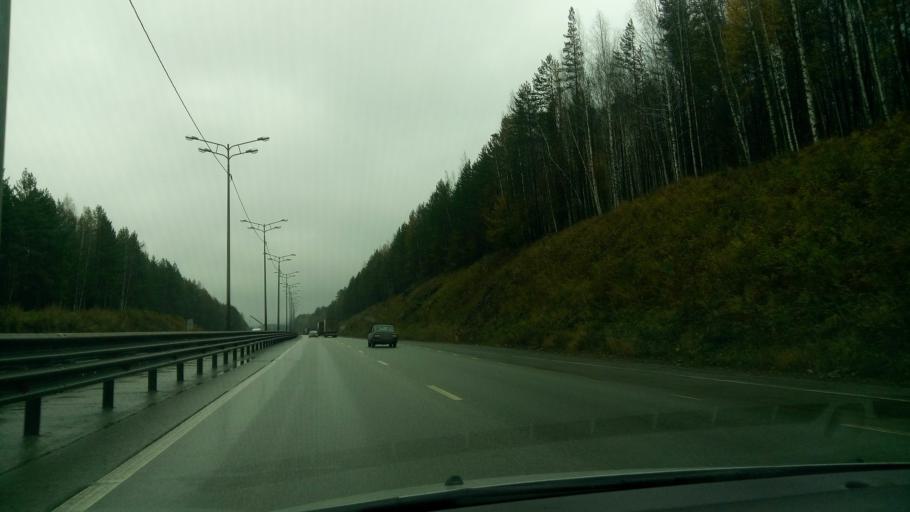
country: RU
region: Sverdlovsk
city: Severka
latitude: 56.8344
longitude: 60.2990
